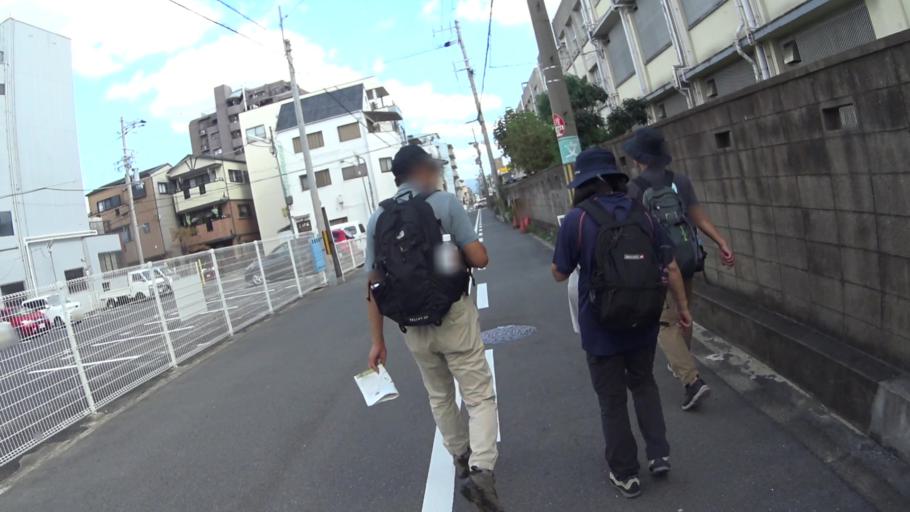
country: JP
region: Osaka
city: Yao
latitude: 34.6473
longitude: 135.5527
